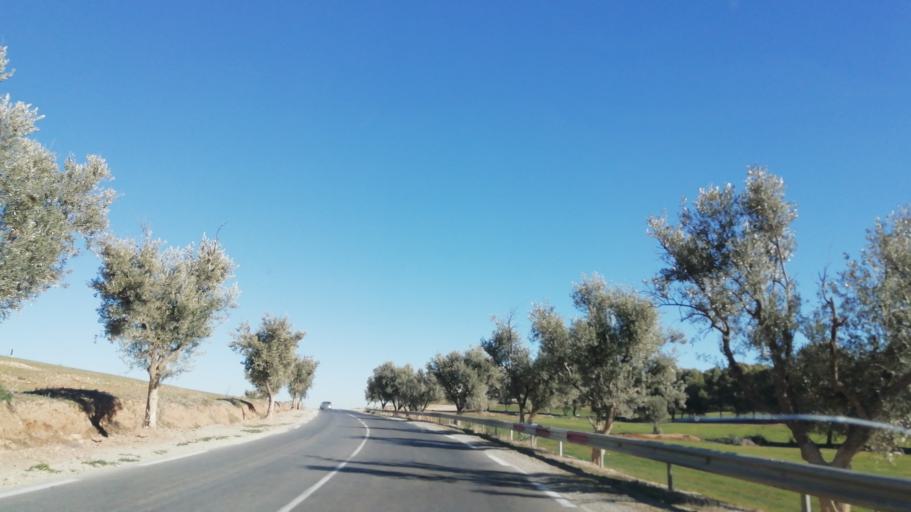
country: DZ
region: Mascara
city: Mascara
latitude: 35.2447
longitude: 0.1200
